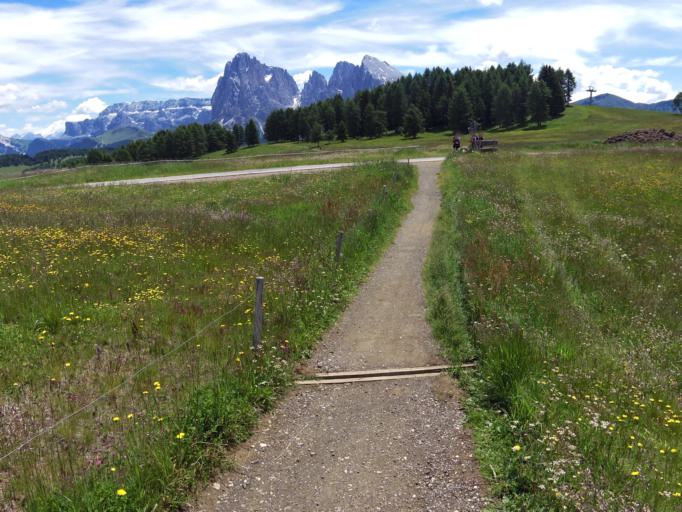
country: IT
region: Trentino-Alto Adige
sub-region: Bolzano
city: Ortisei
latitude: 46.5503
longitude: 11.6464
